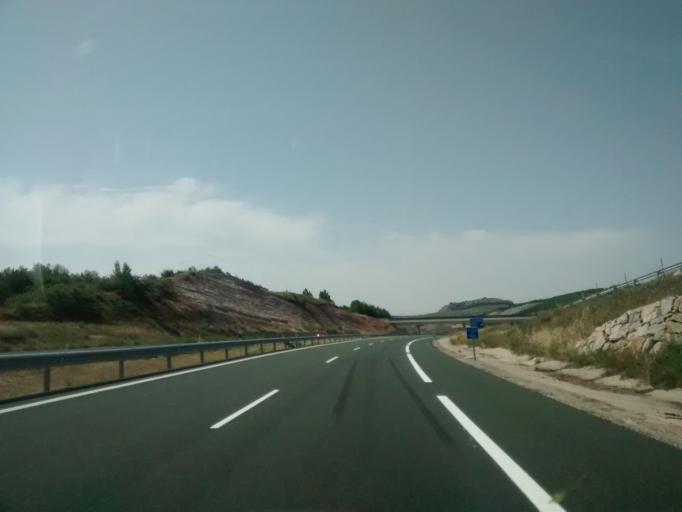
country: ES
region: Castille and Leon
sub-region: Provincia de Palencia
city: Alar del Rey
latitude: 42.7282
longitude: -4.2882
